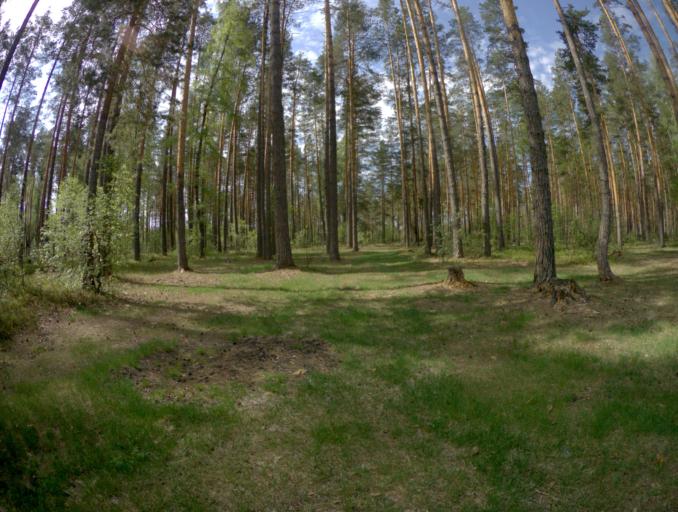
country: RU
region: Ivanovo
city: Yuzha
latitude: 56.5096
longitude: 42.1265
